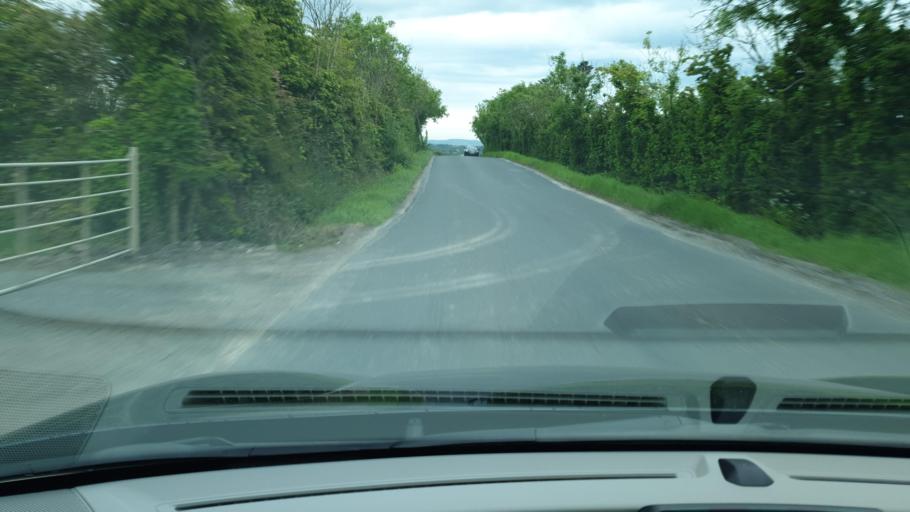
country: IE
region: Leinster
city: Balrothery
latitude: 53.5531
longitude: -6.2394
